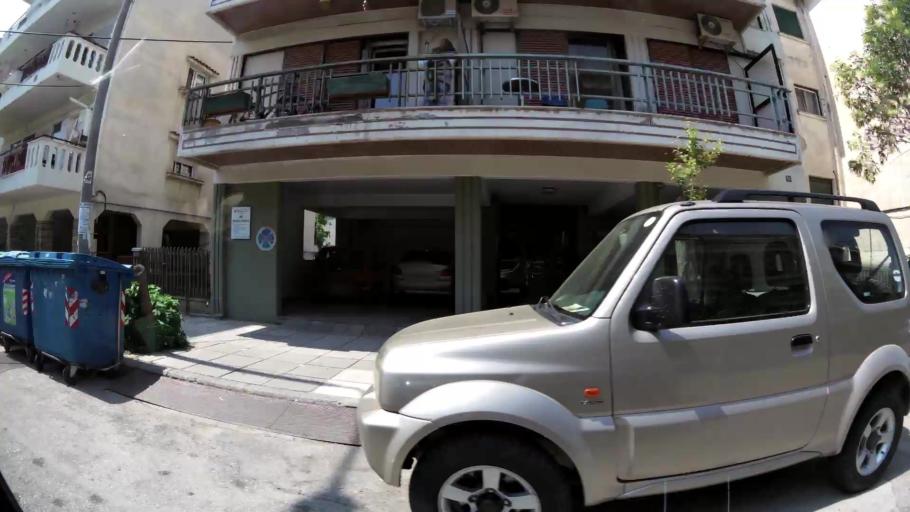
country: GR
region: Central Macedonia
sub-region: Nomos Thessalonikis
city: Agios Pavlos
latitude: 40.6320
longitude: 22.9641
